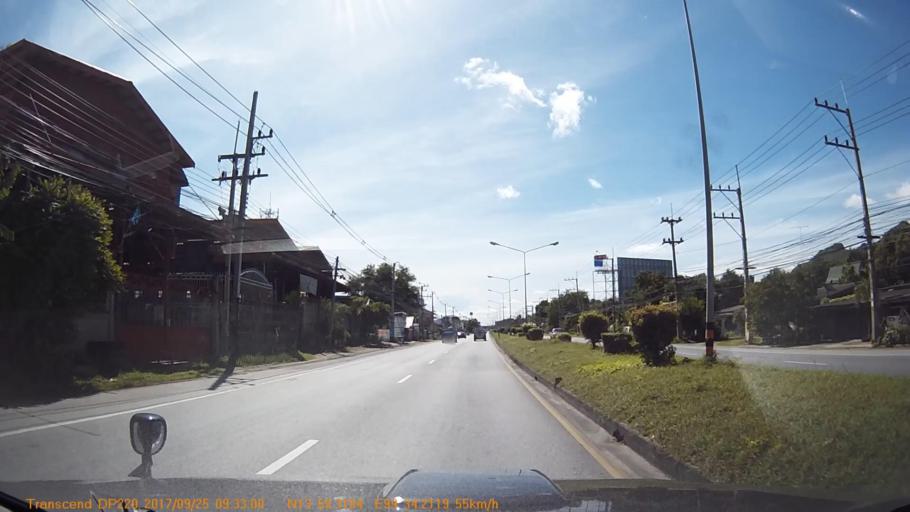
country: TH
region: Kanchanaburi
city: Kanchanaburi
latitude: 13.9885
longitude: 99.5704
